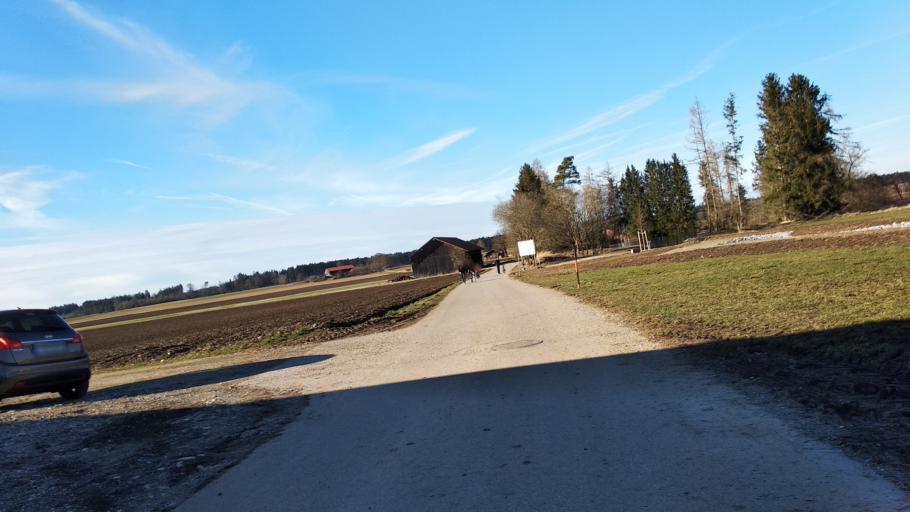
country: DE
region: Bavaria
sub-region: Upper Bavaria
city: Aying
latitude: 47.9740
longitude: 11.7769
